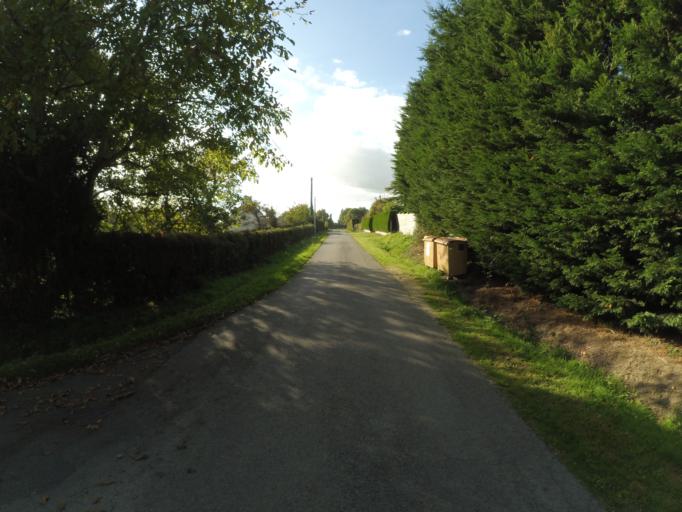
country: FR
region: Brittany
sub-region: Departement du Morbihan
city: Peillac
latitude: 47.7219
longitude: -2.2018
